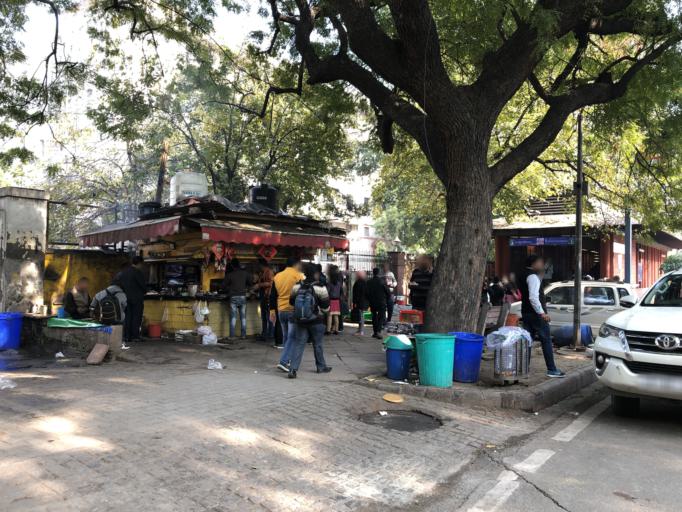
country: IN
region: NCT
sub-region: New Delhi
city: New Delhi
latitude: 28.6177
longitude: 77.2112
